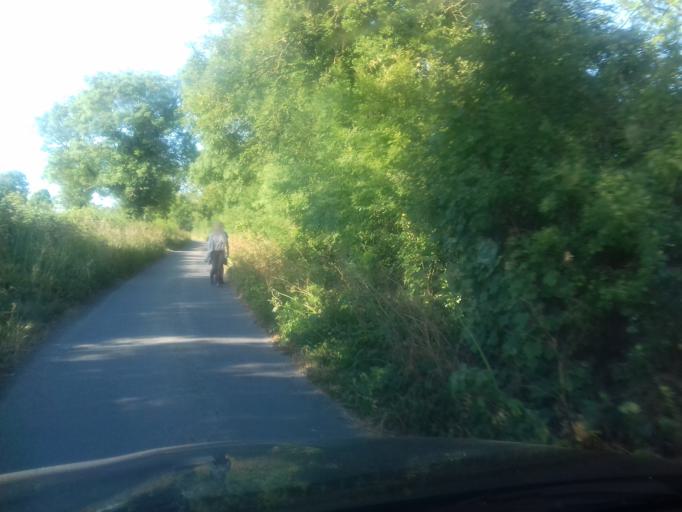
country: IE
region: Leinster
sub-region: Fingal County
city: Blanchardstown
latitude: 53.4340
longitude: -6.3684
